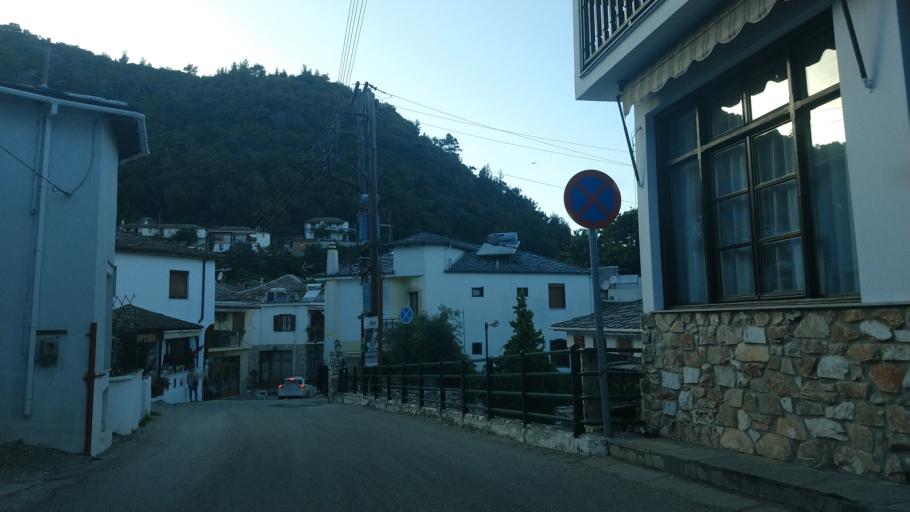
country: GR
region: East Macedonia and Thrace
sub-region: Nomos Kavalas
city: Potamia
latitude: 40.7307
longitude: 24.7297
